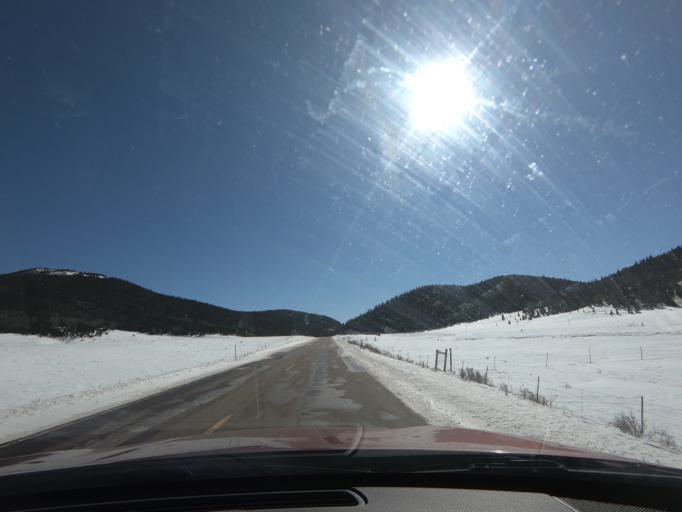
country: US
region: Colorado
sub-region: Teller County
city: Cripple Creek
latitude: 38.7599
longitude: -105.1106
